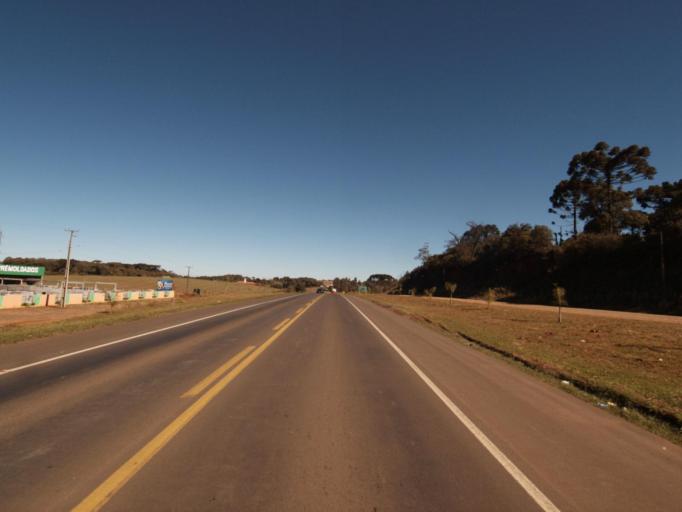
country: BR
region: Santa Catarina
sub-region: Xanxere
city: Xanxere
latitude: -26.8616
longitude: -52.2689
